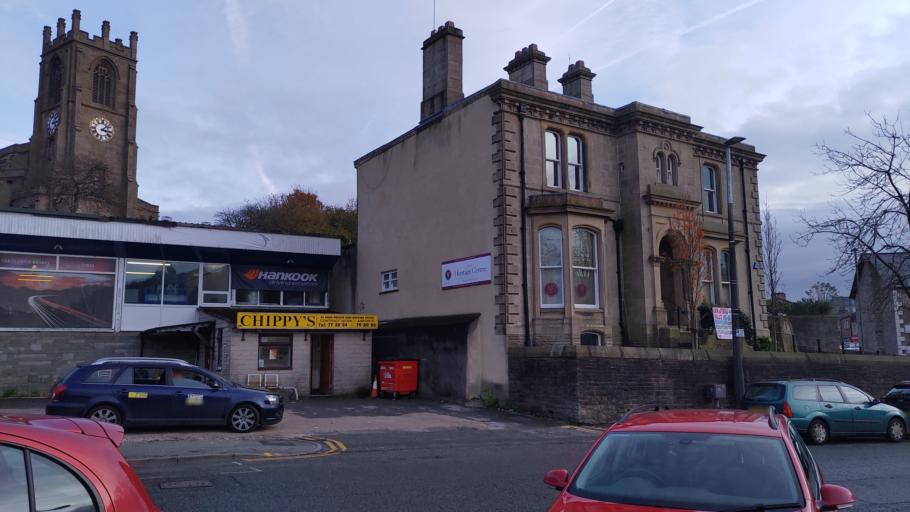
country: GB
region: England
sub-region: Blackburn with Darwen
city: Darwen
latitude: 53.6958
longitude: -2.4658
